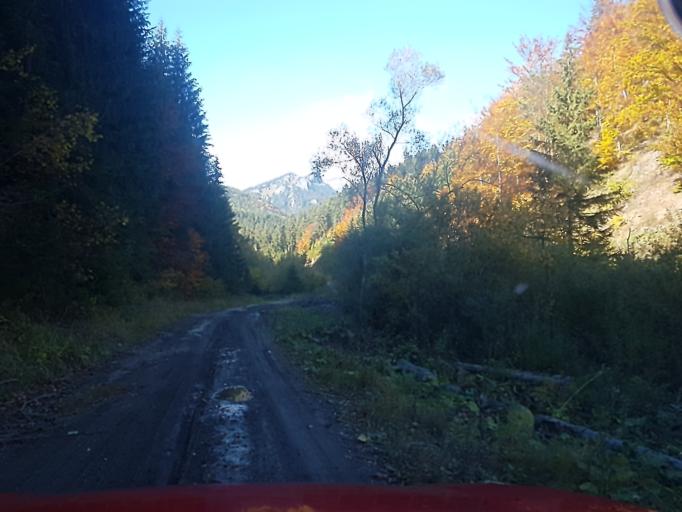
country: SK
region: Zilinsky
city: Ruzomberok
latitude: 49.1199
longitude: 19.3573
